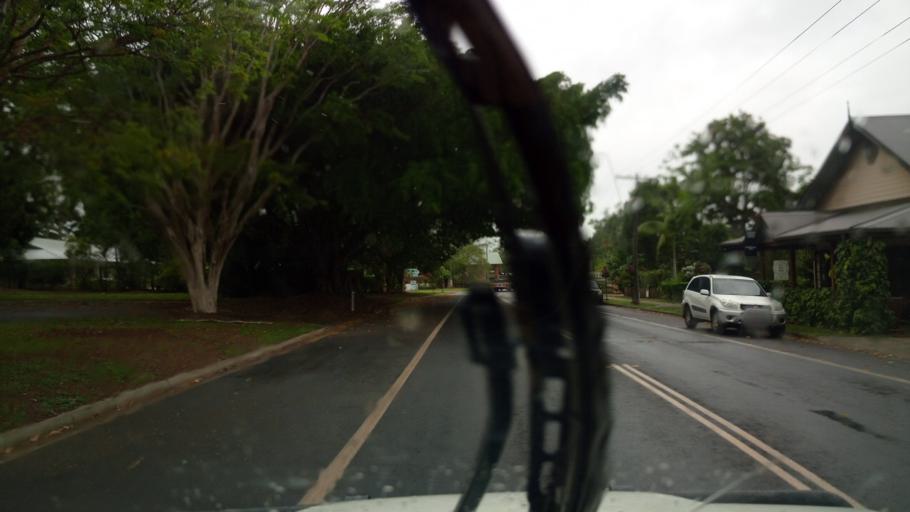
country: AU
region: Queensland
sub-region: Tablelands
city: Tolga
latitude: -17.2721
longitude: 145.5827
